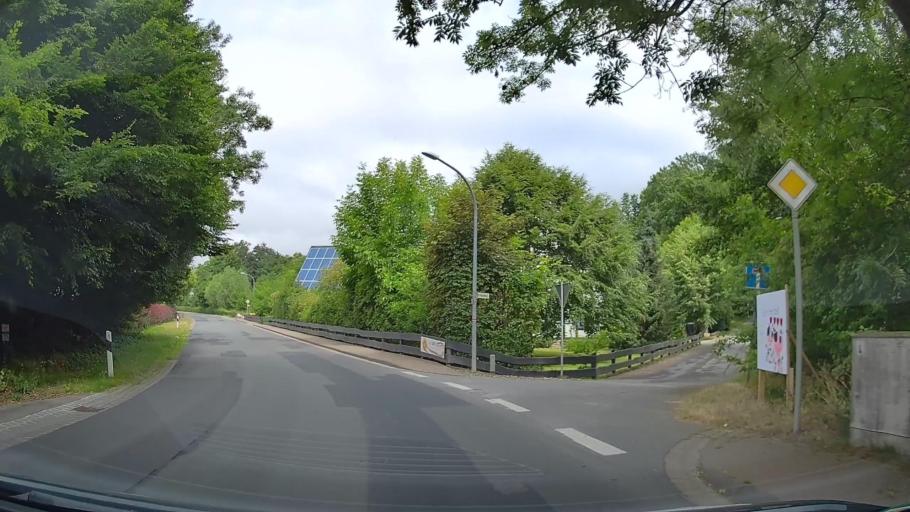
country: DE
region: Lower Saxony
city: Aerzen
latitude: 52.0417
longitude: 9.1983
